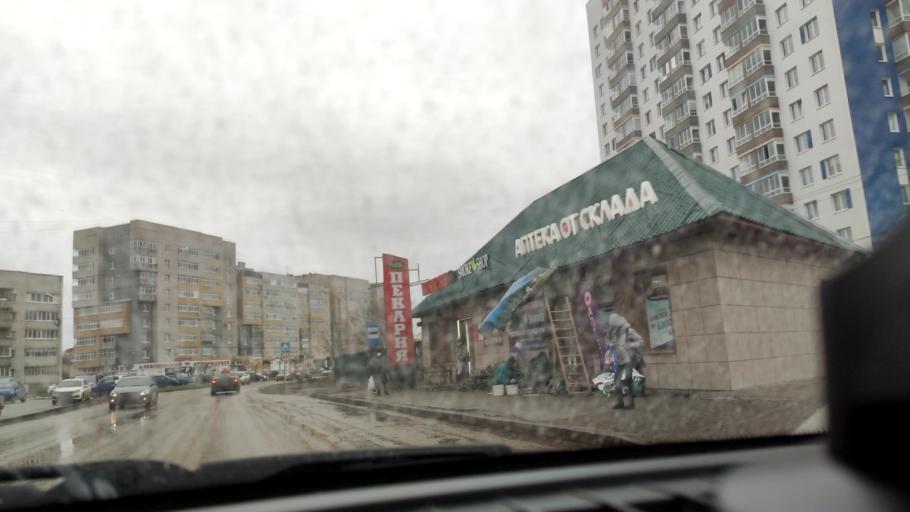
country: RU
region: Perm
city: Kondratovo
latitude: 57.9763
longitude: 56.1089
